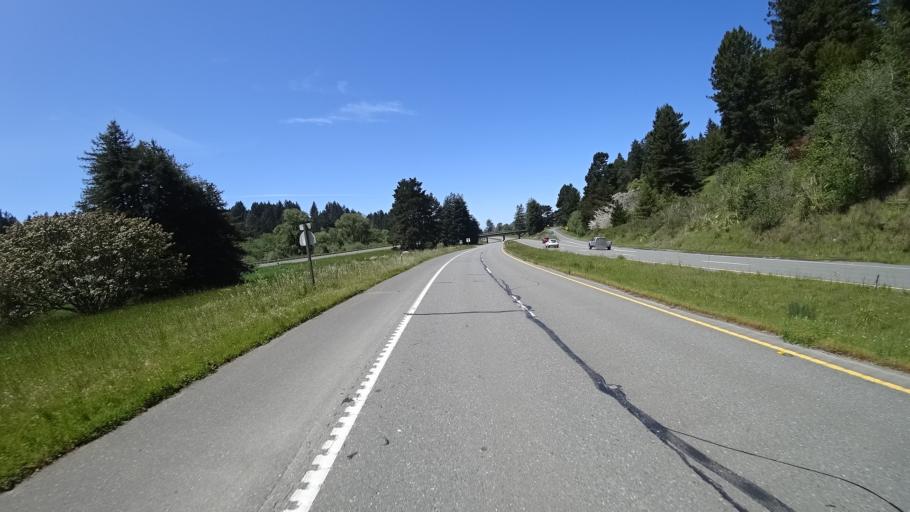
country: US
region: California
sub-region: Humboldt County
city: Arcata
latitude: 40.9094
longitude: -124.0551
